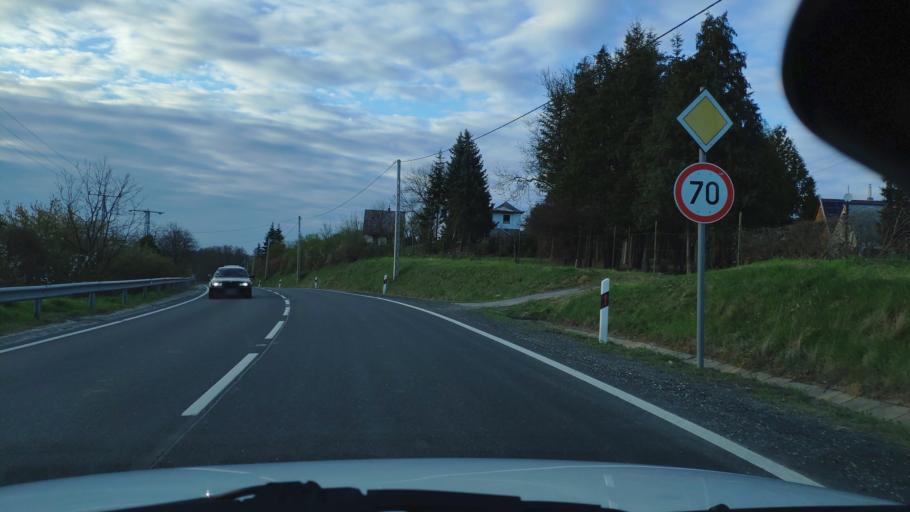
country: HU
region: Zala
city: Nagykanizsa
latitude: 46.4352
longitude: 17.0385
